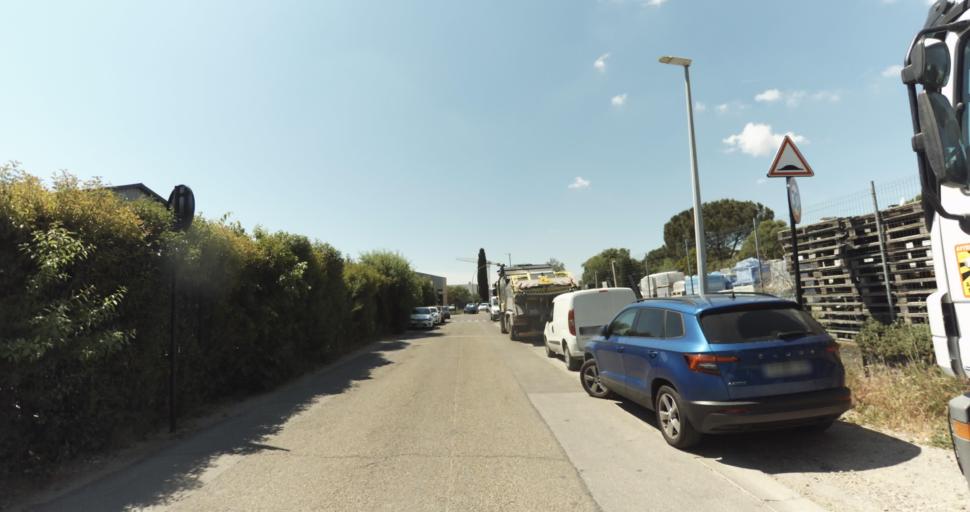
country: FR
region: Languedoc-Roussillon
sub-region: Departement du Gard
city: Milhaud
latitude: 43.8173
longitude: 4.3193
